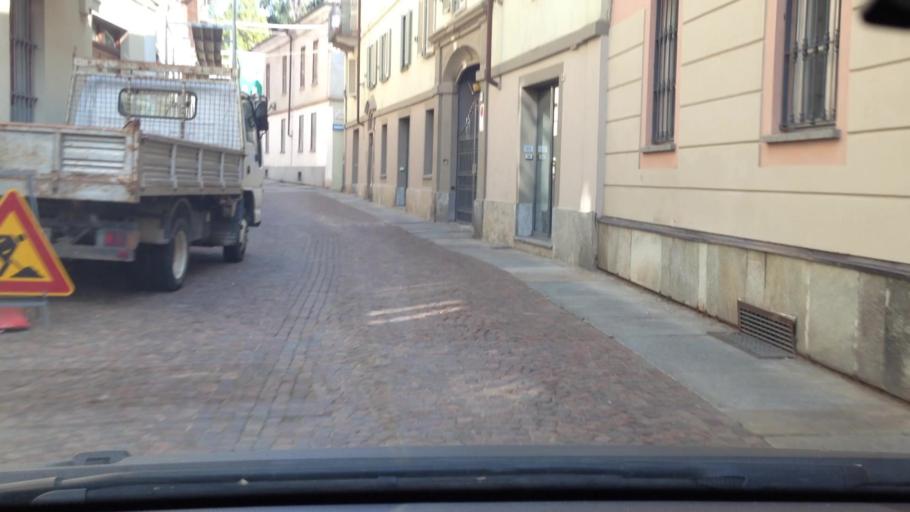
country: IT
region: Piedmont
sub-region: Provincia di Asti
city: Asti
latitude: 44.8968
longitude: 8.2011
